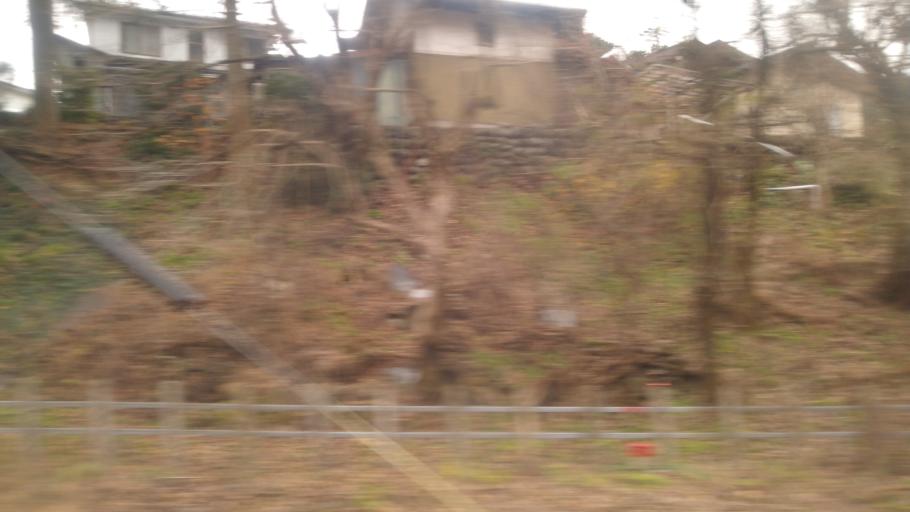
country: JP
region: Nagano
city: Ina
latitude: 35.8721
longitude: 137.7438
